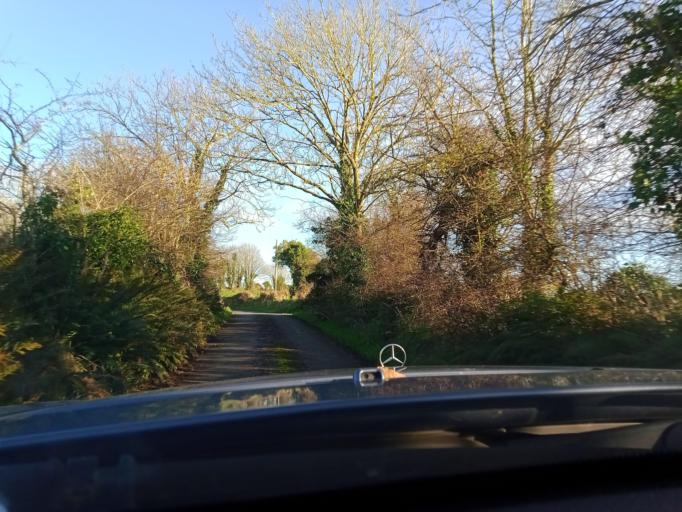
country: IE
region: Leinster
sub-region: Kilkenny
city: Mooncoin
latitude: 52.2644
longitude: -7.2420
